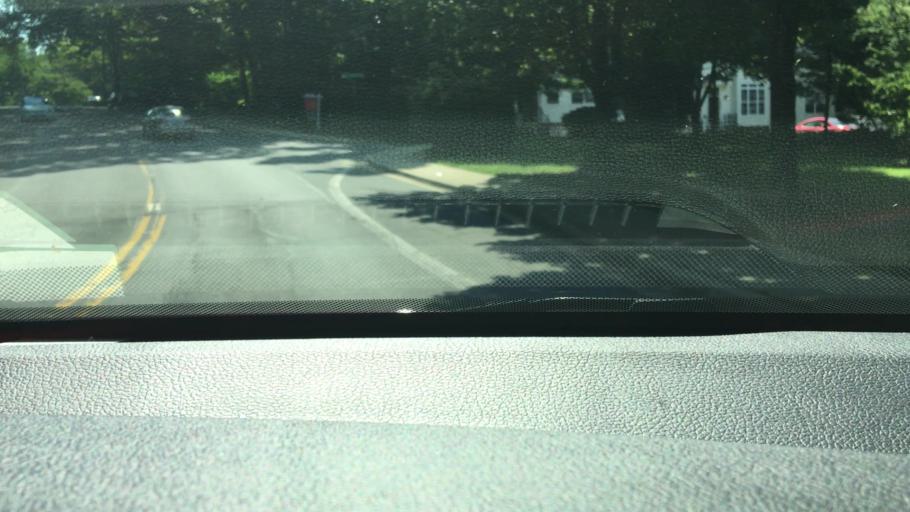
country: US
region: Maryland
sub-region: Montgomery County
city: North Kensington
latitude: 39.0293
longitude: -77.0691
